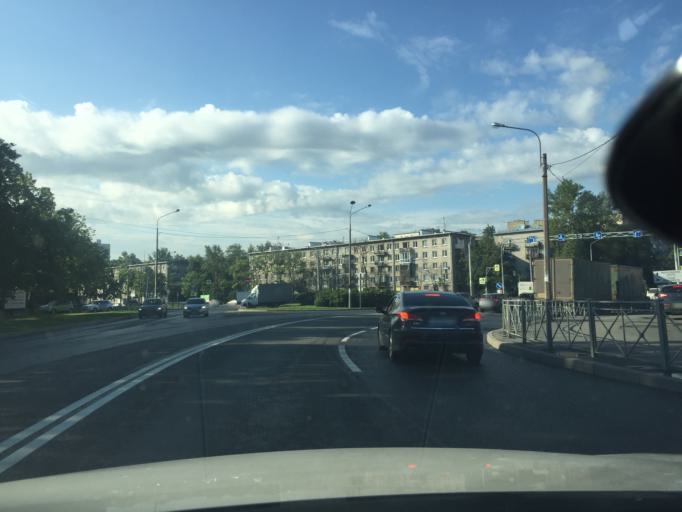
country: RU
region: St.-Petersburg
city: Kupchino
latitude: 59.8401
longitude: 30.3382
